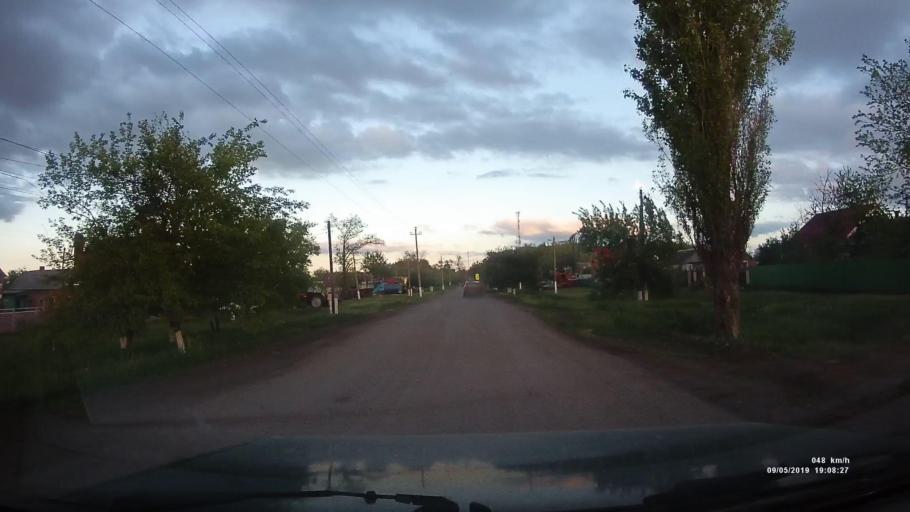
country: RU
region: Krasnodarskiy
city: Kanelovskaya
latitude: 46.7295
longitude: 39.2040
